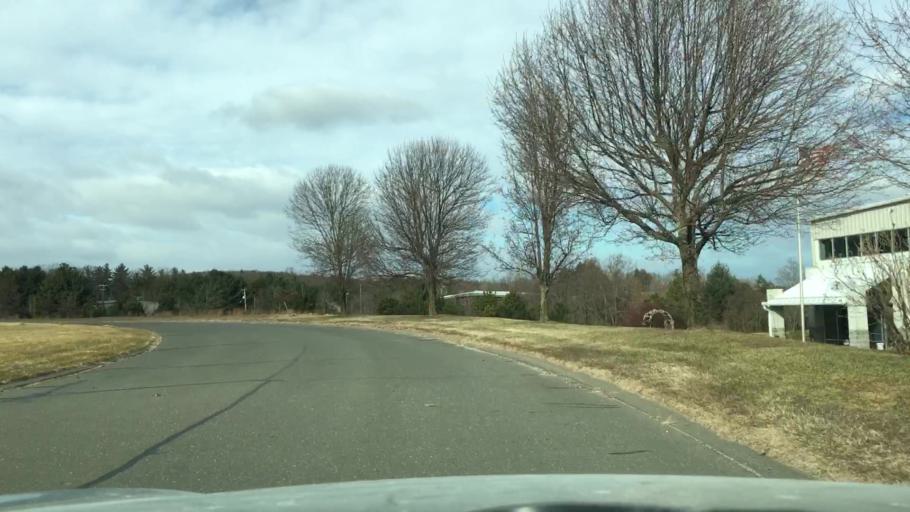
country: US
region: Massachusetts
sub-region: Hampden County
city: Southwick
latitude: 42.0694
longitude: -72.7431
